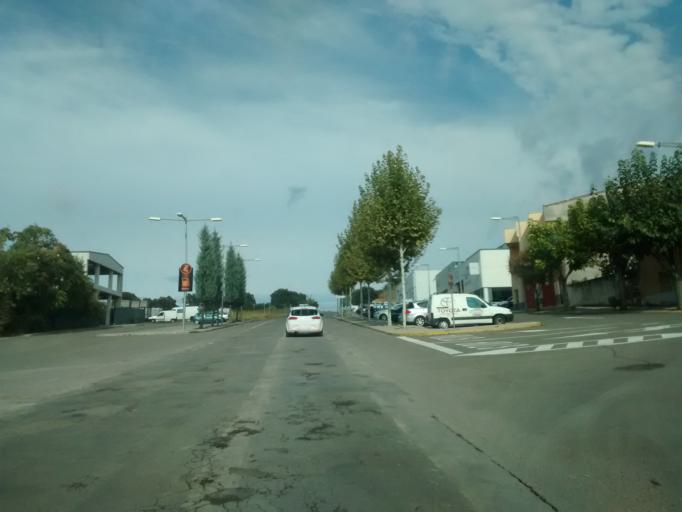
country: ES
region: Aragon
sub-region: Provincia de Huesca
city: Barbastro
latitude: 42.0426
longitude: 0.1364
